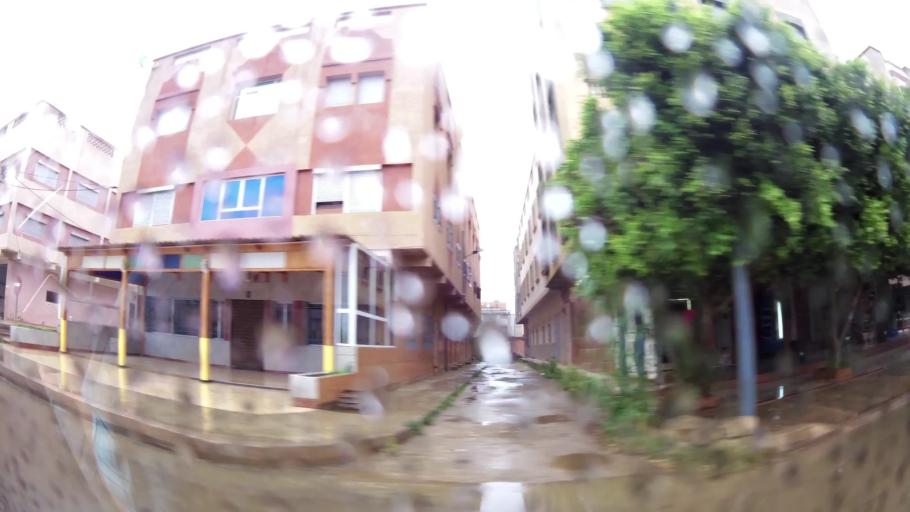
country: MA
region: Oriental
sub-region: Nador
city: Boudinar
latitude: 35.1144
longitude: -3.6416
